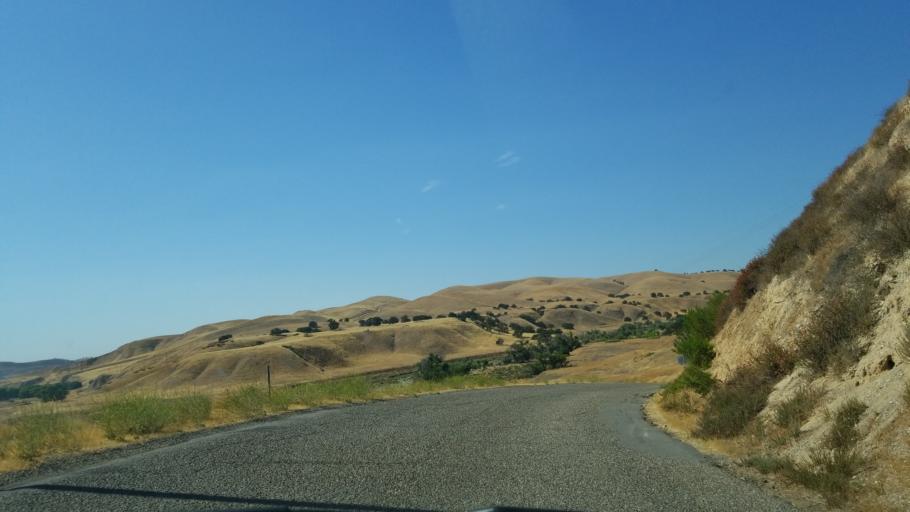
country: US
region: California
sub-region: San Luis Obispo County
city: San Miguel
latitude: 35.7905
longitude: -120.7182
